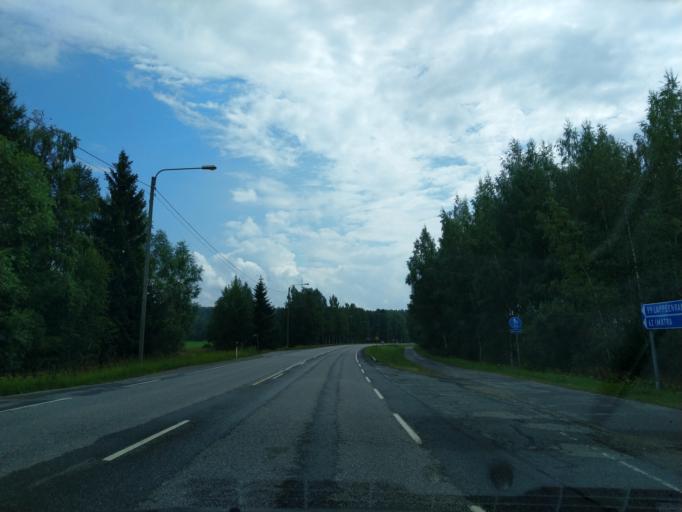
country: FI
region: South Karelia
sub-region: Imatra
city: Parikkala
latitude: 61.5773
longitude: 29.5030
